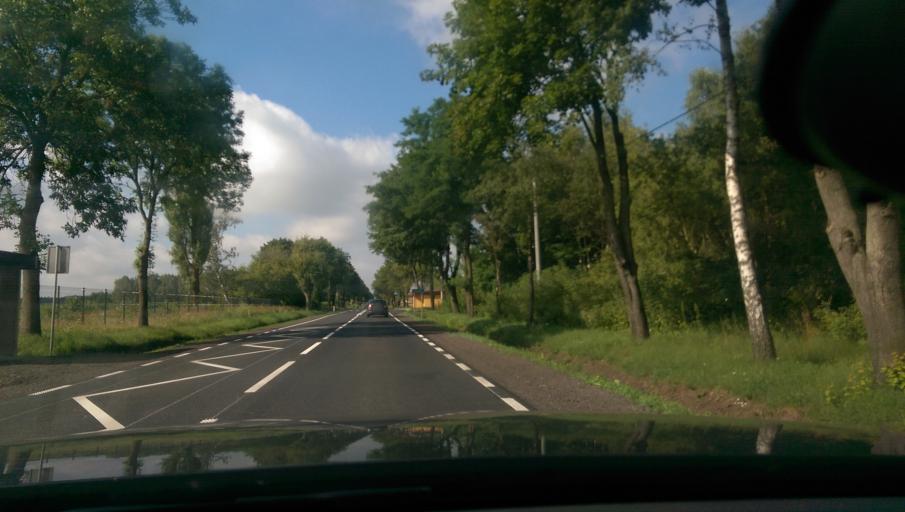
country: PL
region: Masovian Voivodeship
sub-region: Powiat ciechanowski
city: Ojrzen
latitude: 52.7468
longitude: 20.5287
